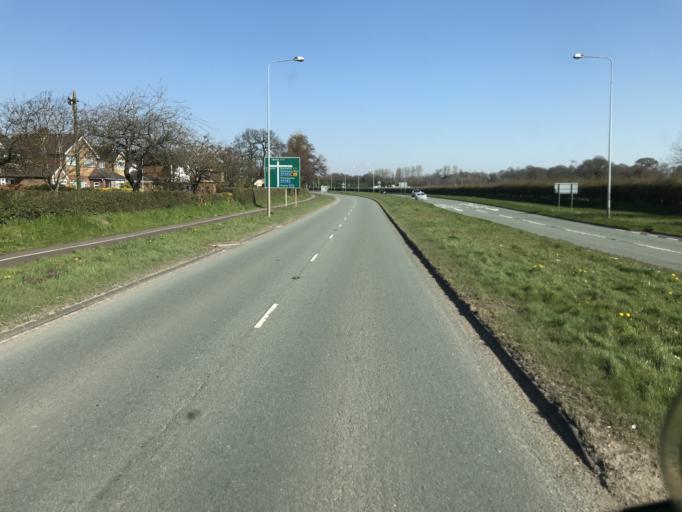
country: GB
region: England
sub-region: Cheshire West and Chester
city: Guilden Sutton
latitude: 53.1909
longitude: -2.8505
